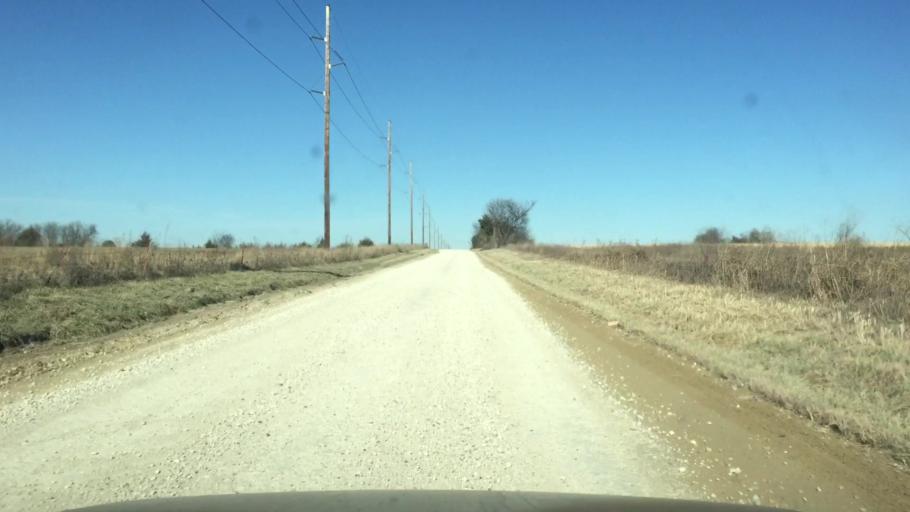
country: US
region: Kansas
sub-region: Allen County
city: Humboldt
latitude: 37.8318
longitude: -95.4185
